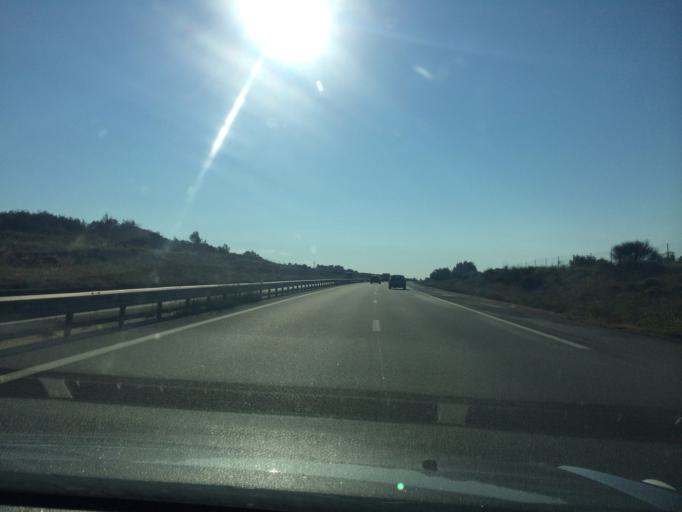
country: FR
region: Languedoc-Roussillon
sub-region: Departement de l'Herault
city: Murviel-les-Montpellier
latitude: 43.6329
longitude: 3.7302
